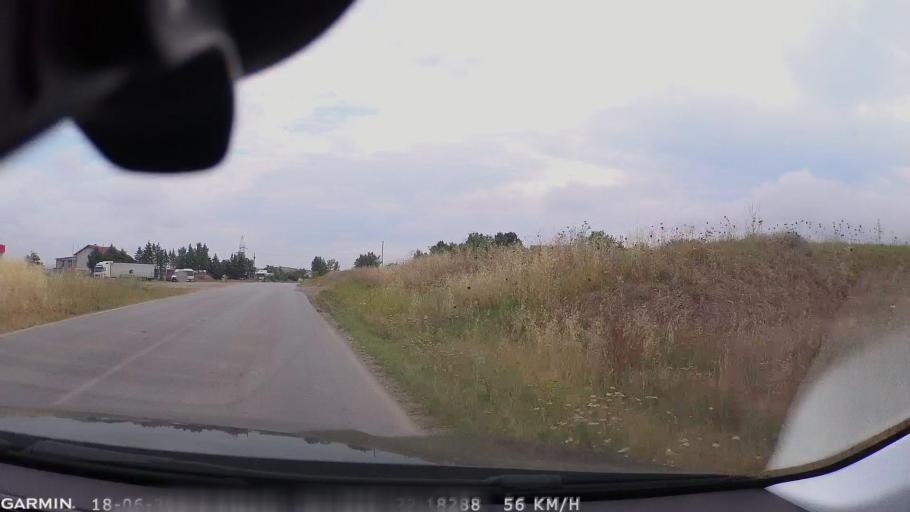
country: MK
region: Stip
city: Shtip
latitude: 41.7747
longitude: 22.1828
